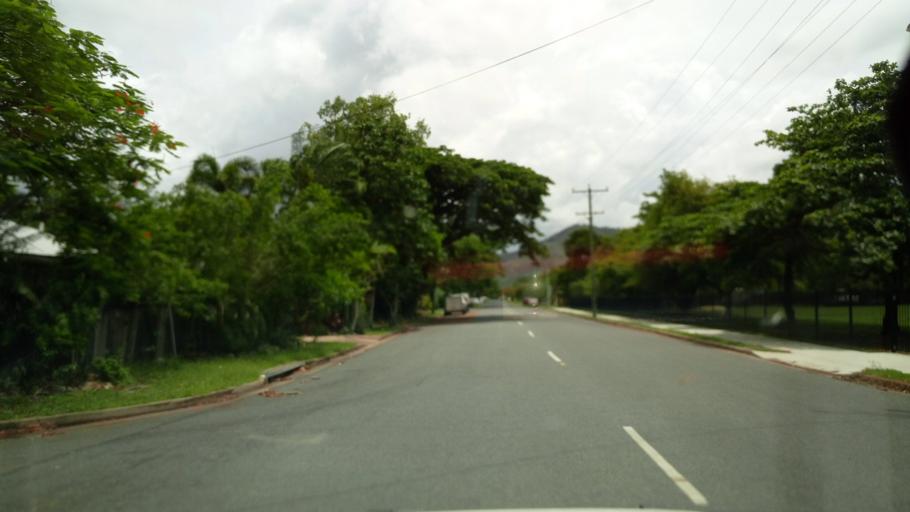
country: AU
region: Queensland
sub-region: Cairns
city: Redlynch
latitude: -16.8531
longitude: 145.7457
